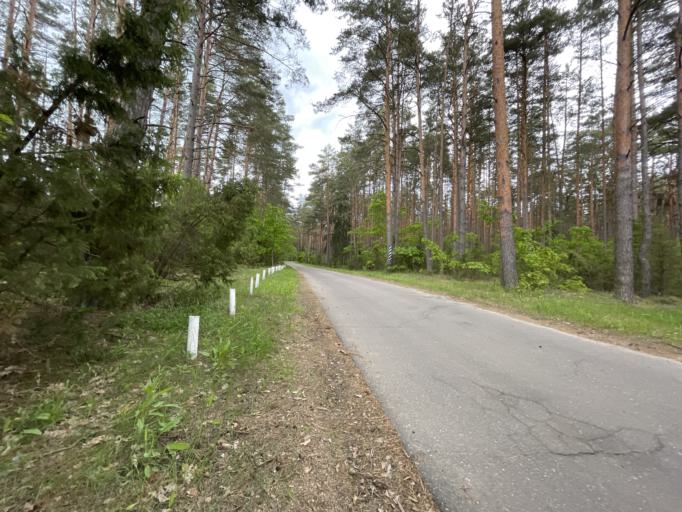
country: BY
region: Minsk
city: Stowbtsy
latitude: 53.4266
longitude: 26.8127
